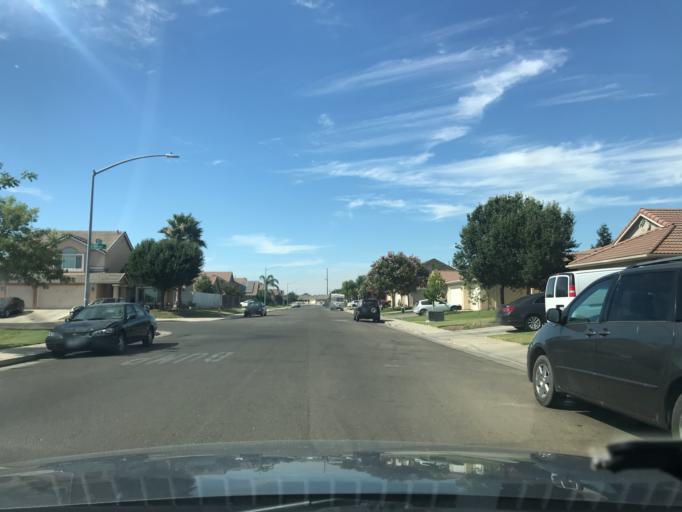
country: US
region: California
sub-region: Merced County
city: Merced
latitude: 37.3257
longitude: -120.5237
